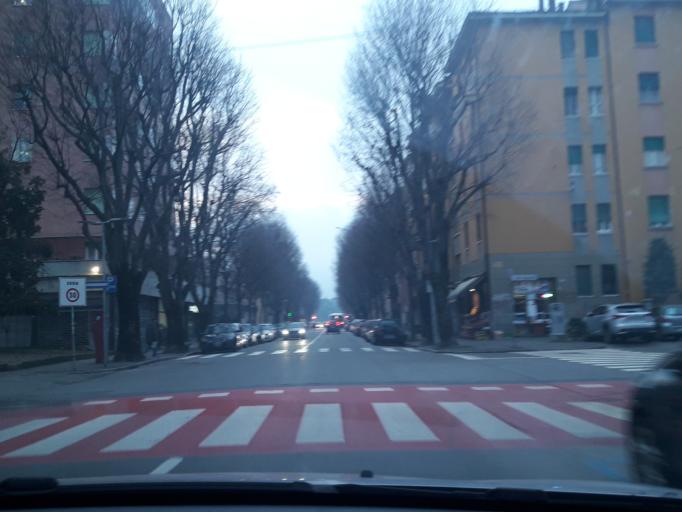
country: IT
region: Emilia-Romagna
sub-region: Provincia di Bologna
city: Bologna
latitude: 44.5028
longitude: 11.3126
